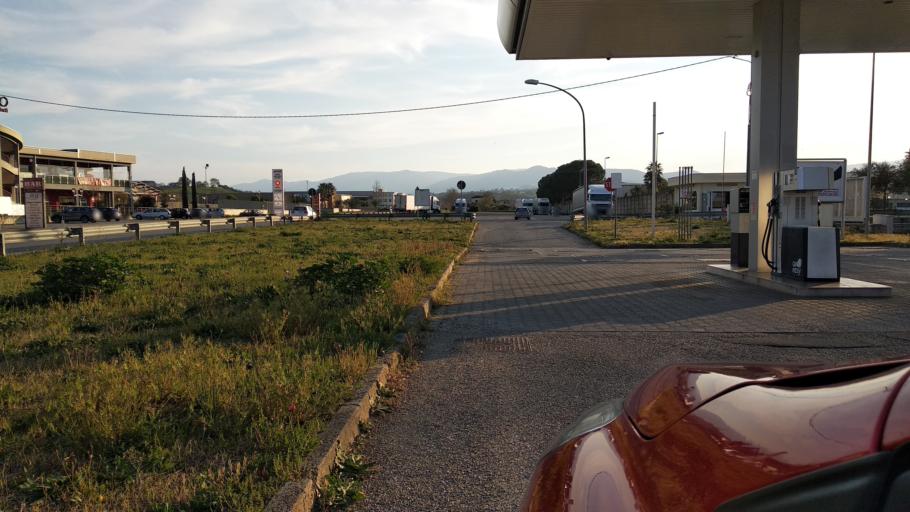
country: IT
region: Calabria
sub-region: Provincia di Cosenza
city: Roggiano Gravina
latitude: 39.5963
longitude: 16.1959
